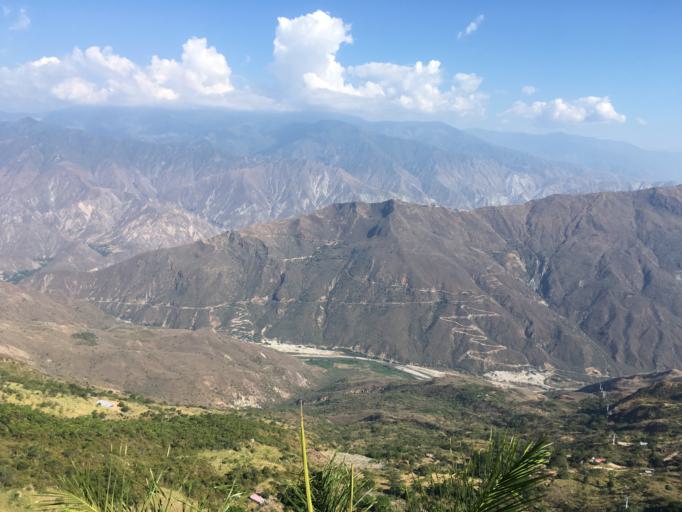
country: CO
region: Santander
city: Aratoca
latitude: 6.8073
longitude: -73.0483
